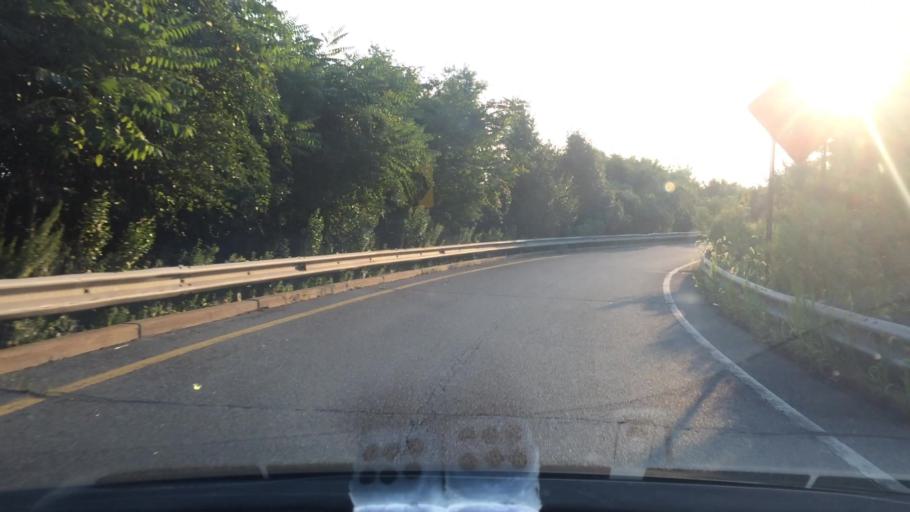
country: US
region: Delaware
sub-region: New Castle County
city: Newport
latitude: 39.7030
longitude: -75.6016
